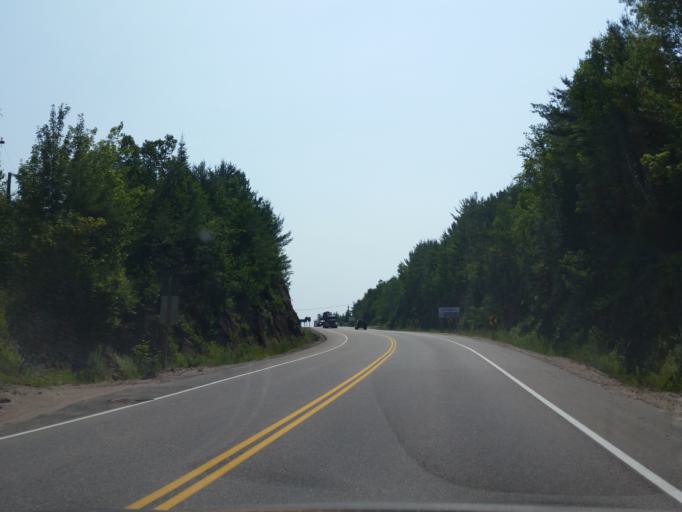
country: CA
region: Ontario
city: Mattawa
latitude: 46.3151
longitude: -78.6888
